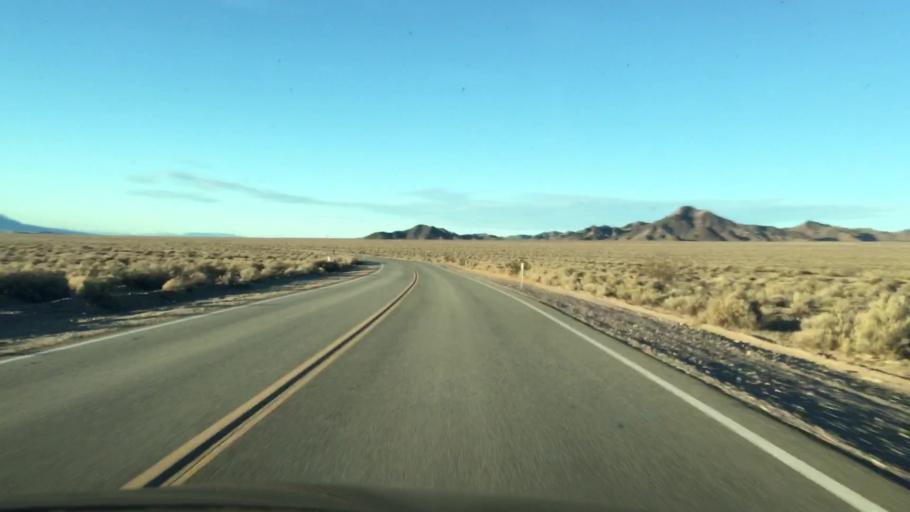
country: US
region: California
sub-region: San Bernardino County
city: Fort Irwin
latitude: 35.3430
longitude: -116.0832
